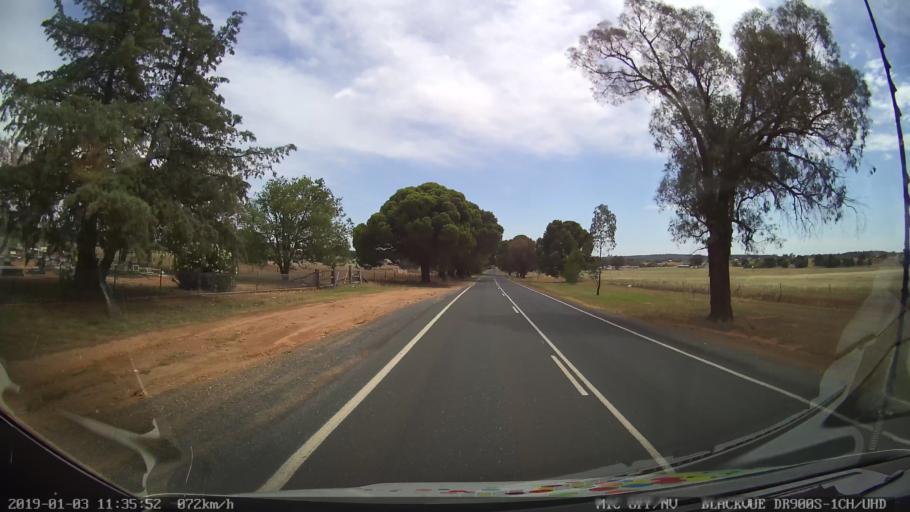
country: AU
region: New South Wales
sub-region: Weddin
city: Grenfell
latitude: -33.9173
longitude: 148.1593
